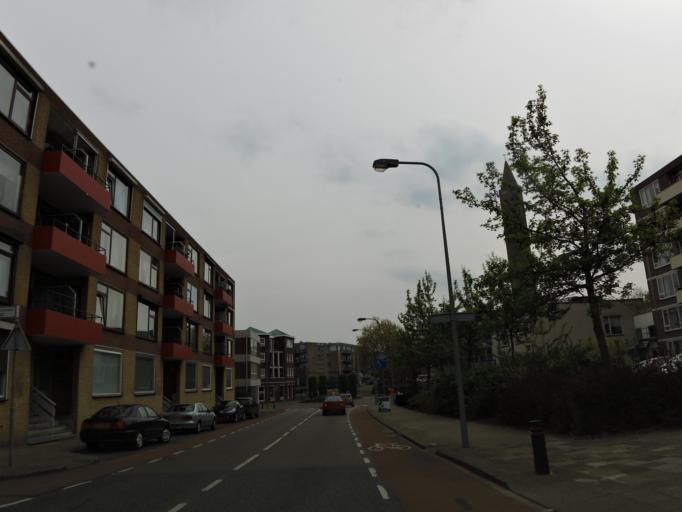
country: NL
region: Limburg
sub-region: Gemeente Brunssum
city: Brunssum
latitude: 50.9510
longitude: 5.9698
